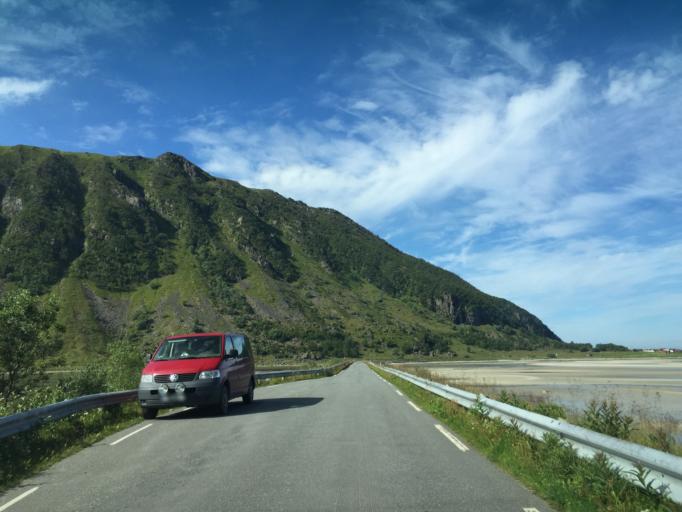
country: NO
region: Nordland
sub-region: Vagan
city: Svolvaer
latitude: 68.3948
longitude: 14.5521
